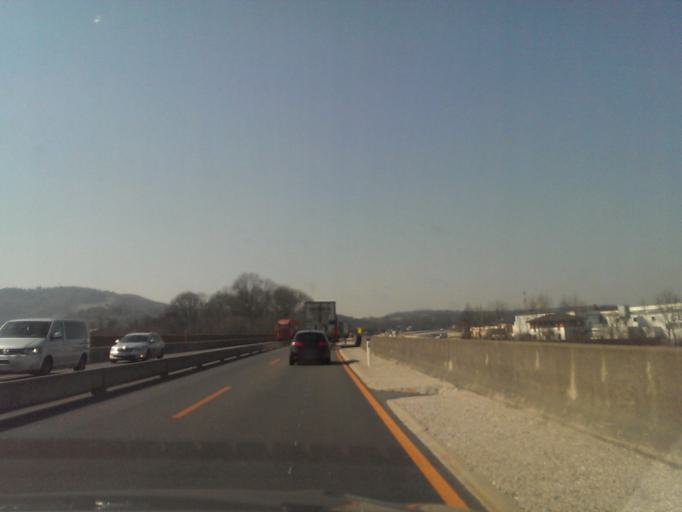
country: AT
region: Upper Austria
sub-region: Politischer Bezirk Vocklabruck
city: Wolfsegg am Hausruck
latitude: 48.1900
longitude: 13.6607
